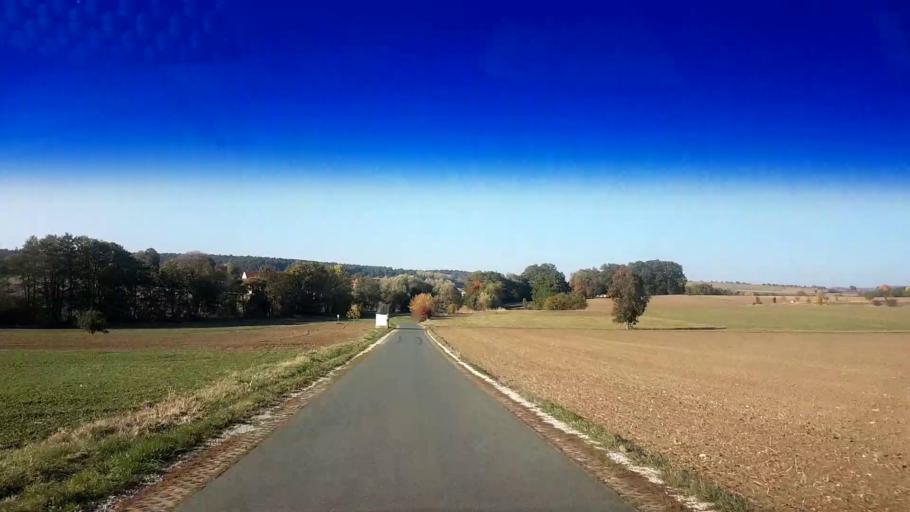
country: DE
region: Bavaria
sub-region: Upper Franconia
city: Strullendorf
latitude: 49.8605
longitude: 10.9988
